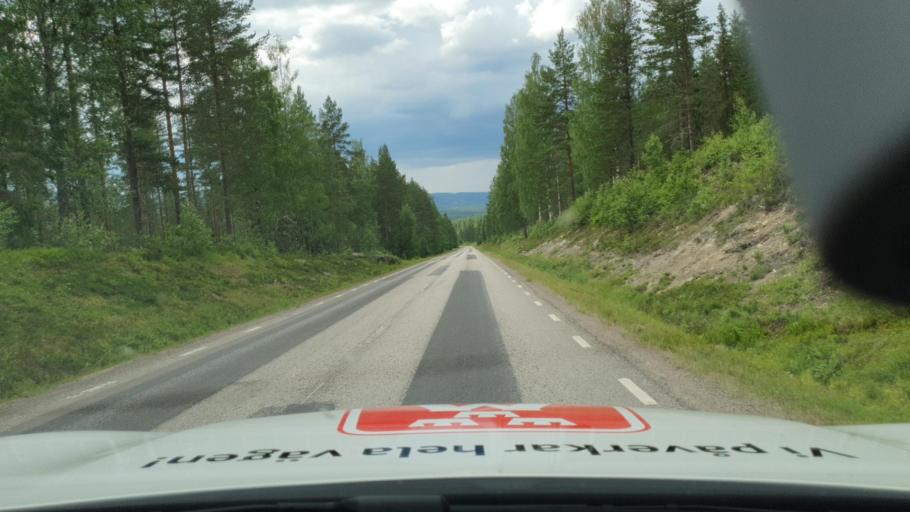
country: NO
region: Hedmark
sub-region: Trysil
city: Innbygda
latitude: 61.0255
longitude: 12.4939
